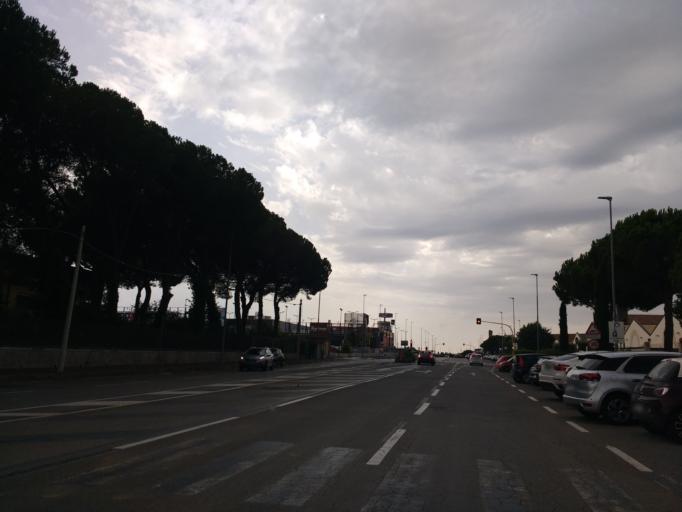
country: IT
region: Latium
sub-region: Citta metropolitana di Roma Capitale
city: Monte Migliore-La Selvotta
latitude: 41.7176
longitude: 12.4469
